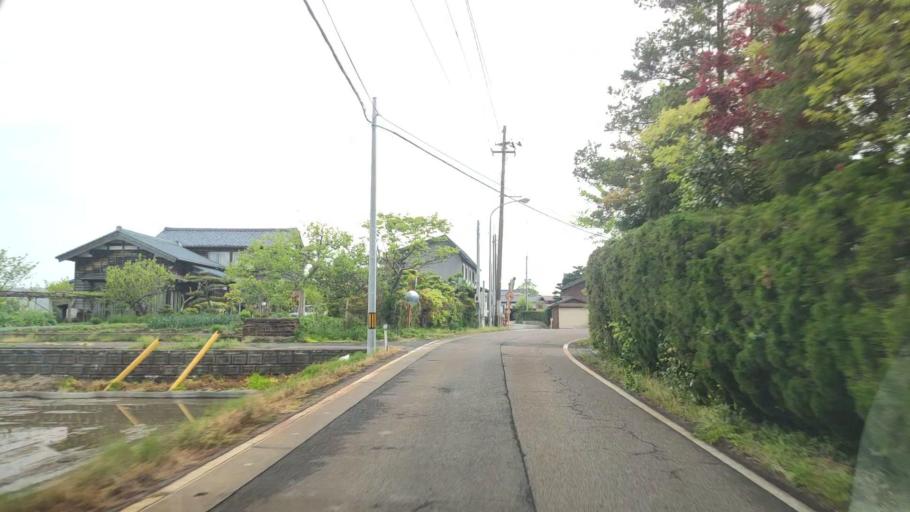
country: JP
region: Niigata
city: Gosen
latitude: 37.7324
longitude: 139.1622
